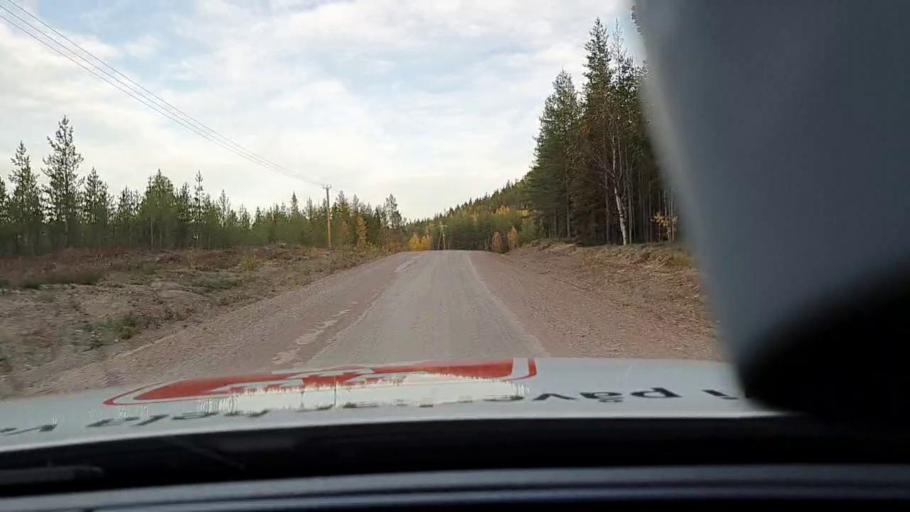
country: SE
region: Norrbotten
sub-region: Overkalix Kommun
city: OEverkalix
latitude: 66.3260
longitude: 22.6089
